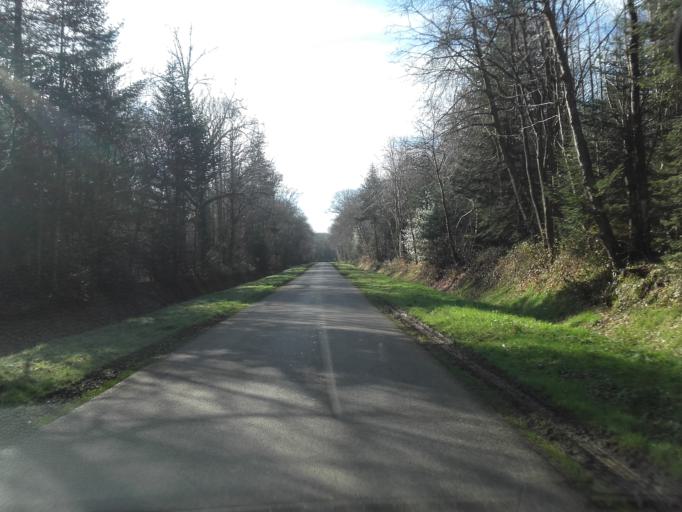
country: FR
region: Brittany
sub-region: Departement des Cotes-d'Armor
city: Pleguien
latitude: 48.6552
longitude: -2.9340
